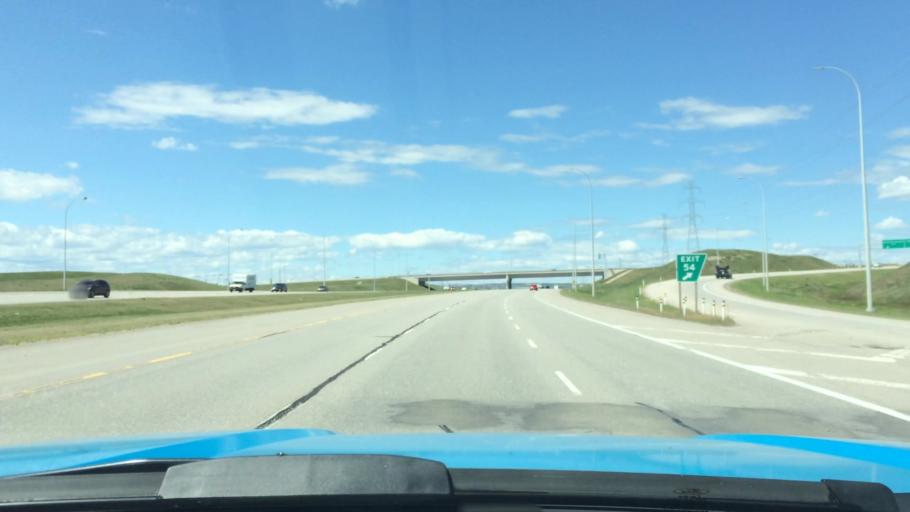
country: CA
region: Alberta
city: Calgary
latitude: 51.1733
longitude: -114.0620
